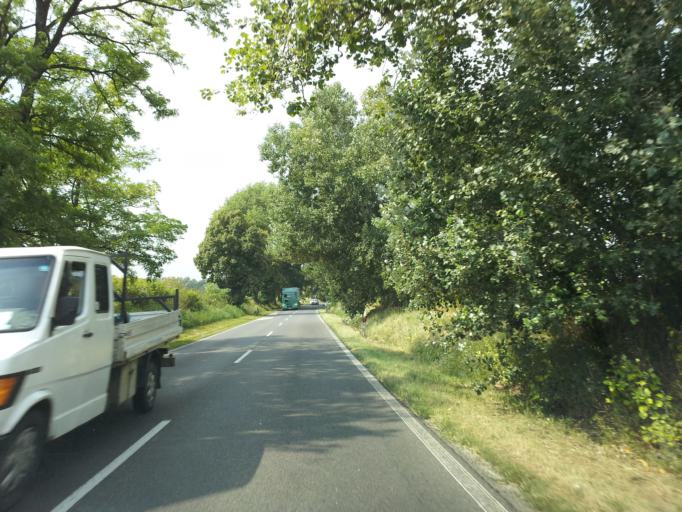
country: HU
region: Gyor-Moson-Sopron
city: Nyul
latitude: 47.5712
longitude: 17.7002
